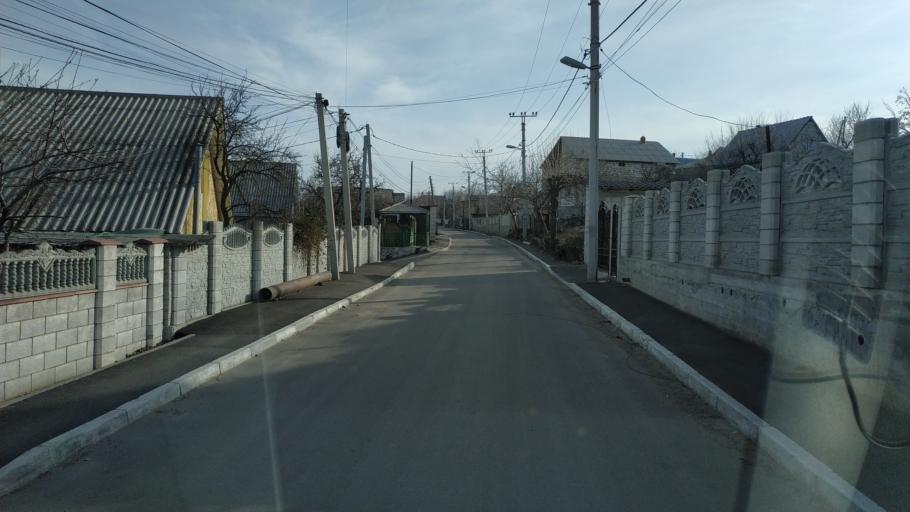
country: MD
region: Chisinau
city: Vatra
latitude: 47.0765
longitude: 28.6704
